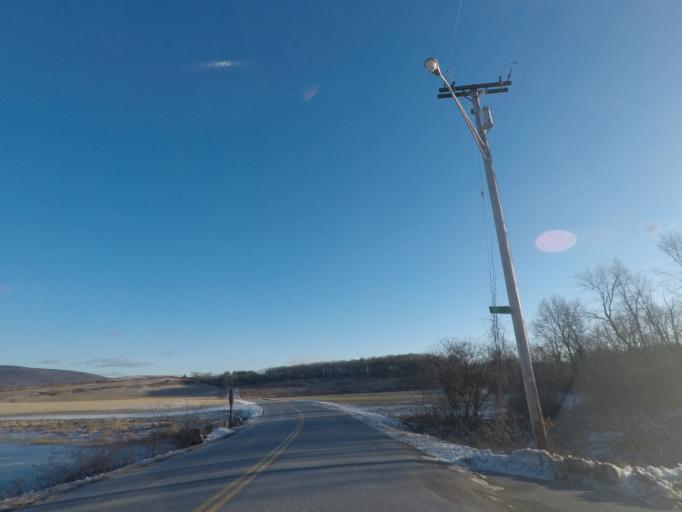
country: US
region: New York
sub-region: Rensselaer County
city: Poestenkill
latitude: 42.7155
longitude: -73.5937
